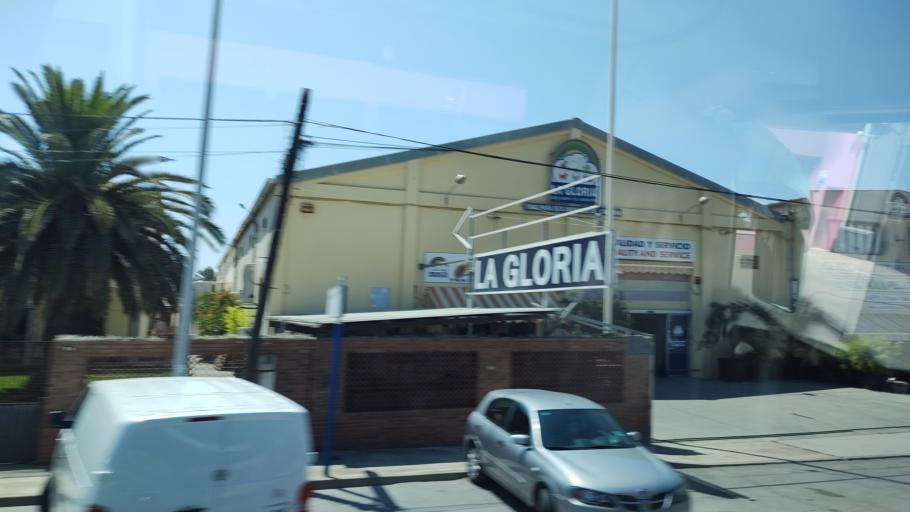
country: ES
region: Andalusia
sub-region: Provincia de Cadiz
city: La Linea de la Concepcion
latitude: 36.1777
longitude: -5.3489
